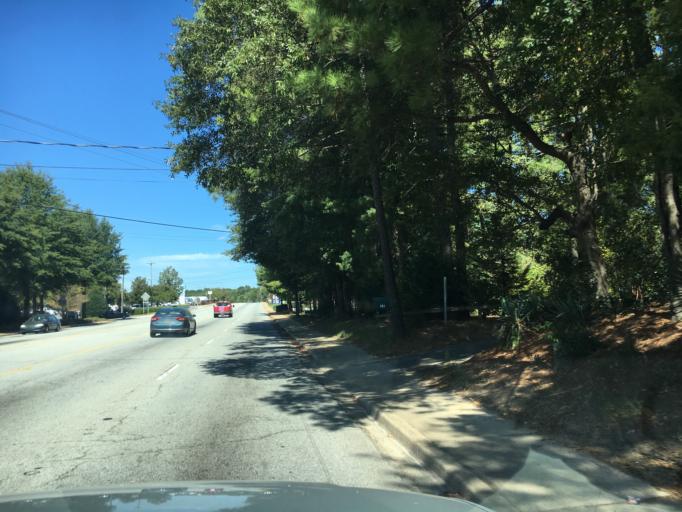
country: US
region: South Carolina
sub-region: Spartanburg County
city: Spartanburg
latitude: 34.9227
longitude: -81.8876
